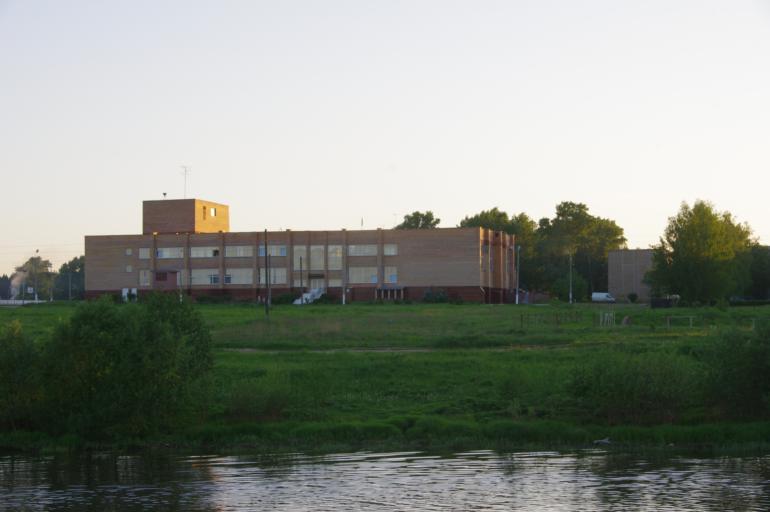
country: RU
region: Moskovskaya
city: Peski
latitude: 55.1941
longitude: 38.7490
